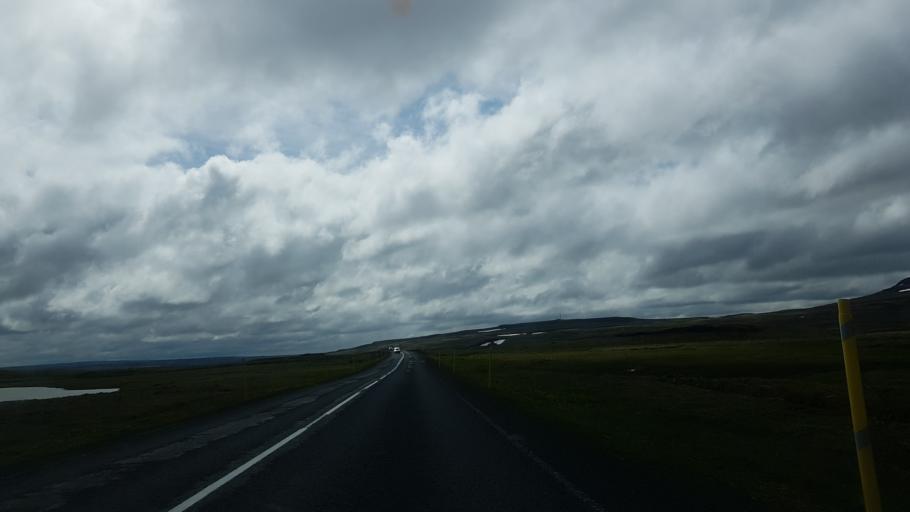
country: IS
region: West
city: Borgarnes
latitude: 64.9803
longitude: -21.0613
